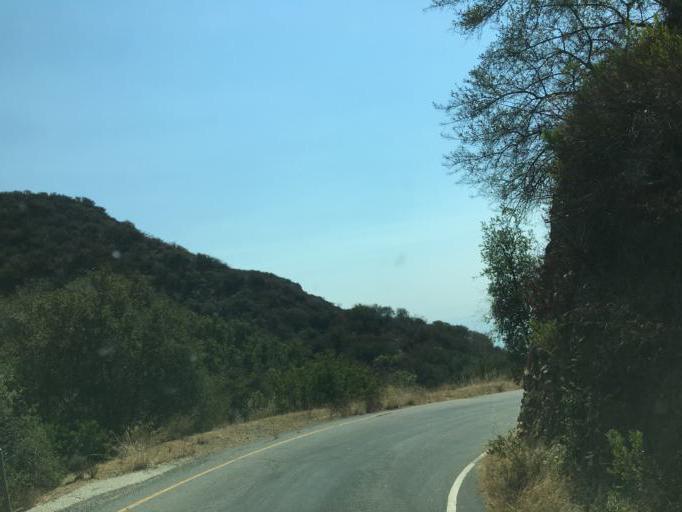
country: US
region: California
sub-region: Los Angeles County
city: Topanga
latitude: 34.0565
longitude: -118.6008
